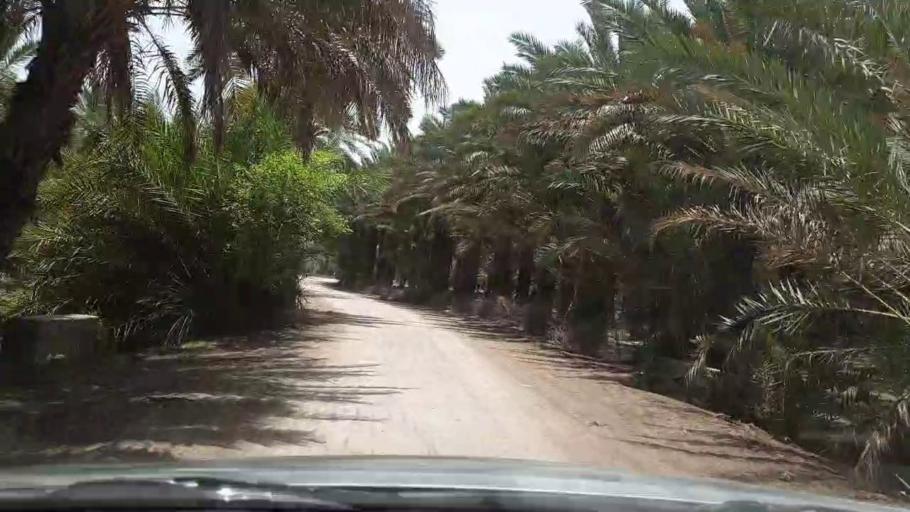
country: PK
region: Sindh
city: Pano Aqil
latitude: 27.8603
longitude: 69.0669
